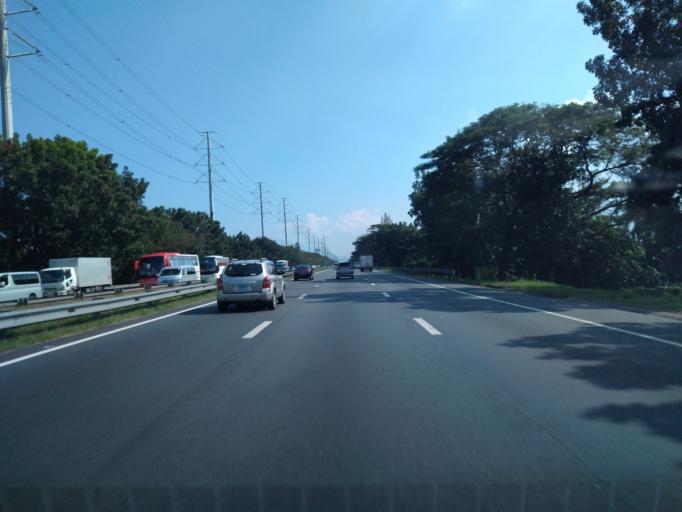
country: PH
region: Calabarzon
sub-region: Province of Laguna
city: Pulong Santa Cruz
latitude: 14.2744
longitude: 121.0939
